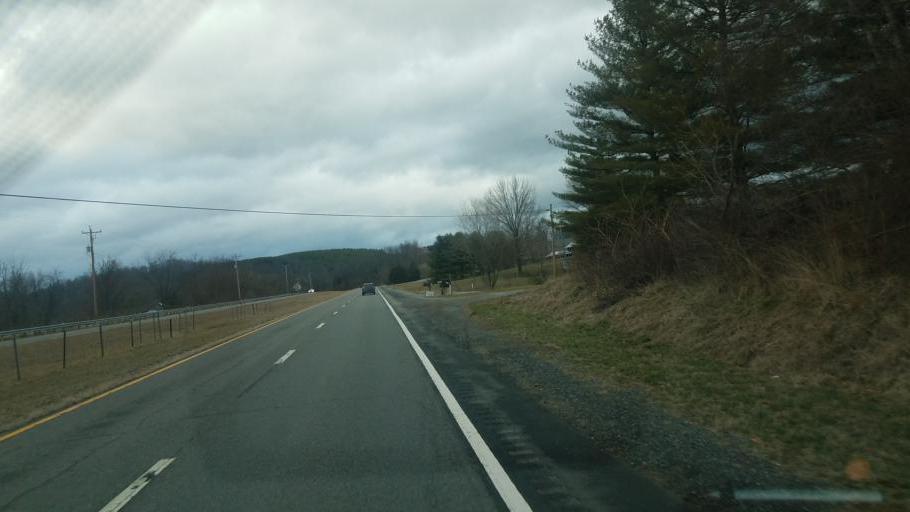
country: US
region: Virginia
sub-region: Giles County
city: Pearisburg
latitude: 37.2602
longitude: -80.7116
